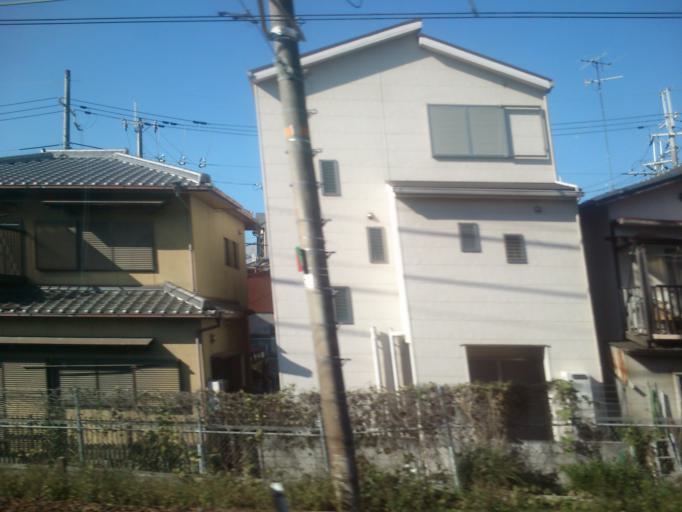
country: JP
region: Kyoto
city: Yawata
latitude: 34.9165
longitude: 135.6974
